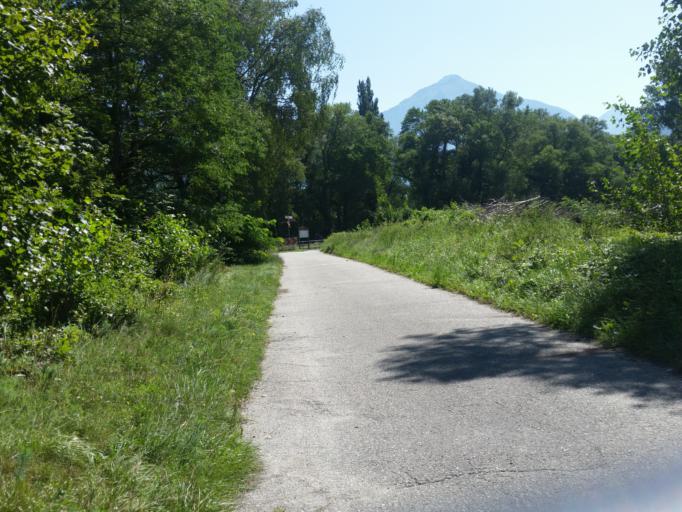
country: CH
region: Valais
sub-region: Saint-Maurice District
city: Vernayaz
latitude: 46.1379
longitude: 7.0507
